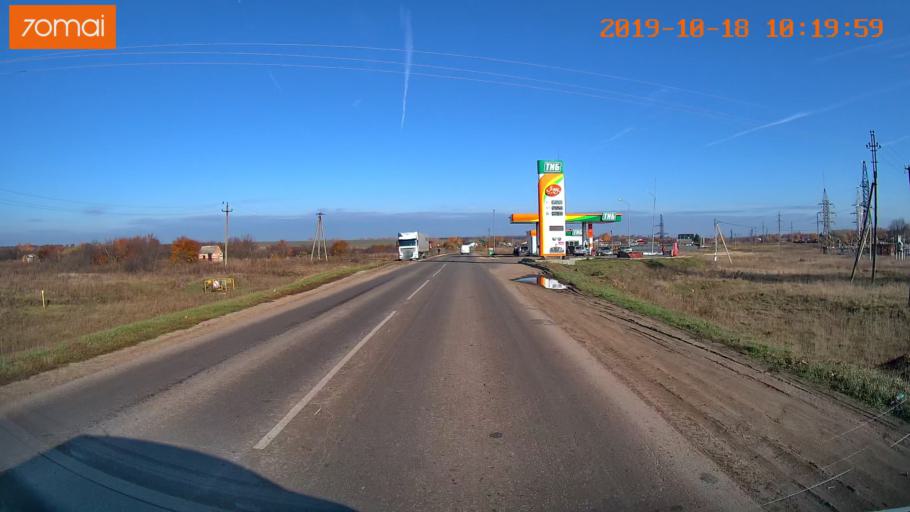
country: RU
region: Tula
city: Kurkino
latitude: 53.4257
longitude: 38.6448
